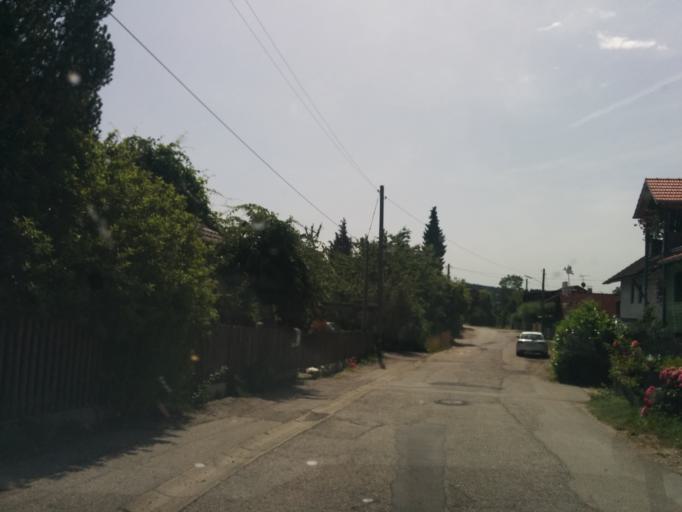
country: DE
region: Bavaria
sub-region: Upper Bavaria
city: Wessling
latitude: 48.0736
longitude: 11.2661
